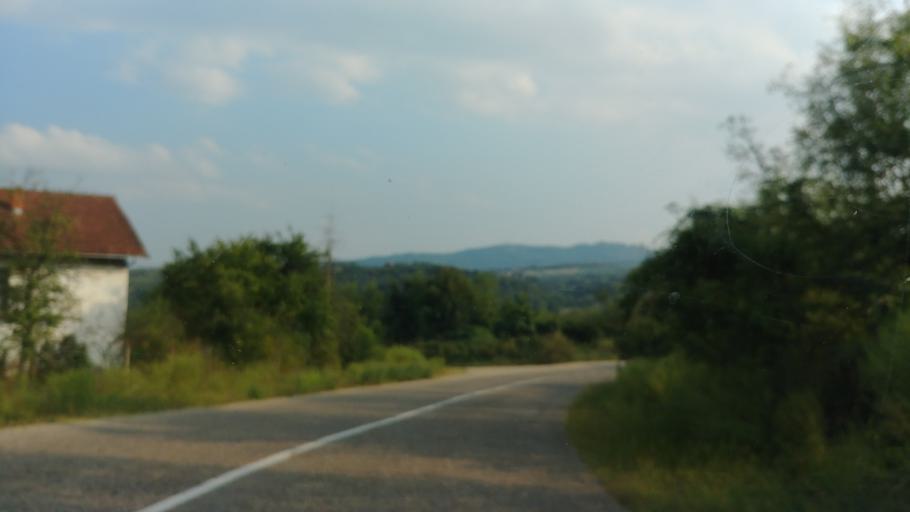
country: BA
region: Republika Srpska
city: Lopare
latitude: 44.7220
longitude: 18.8858
